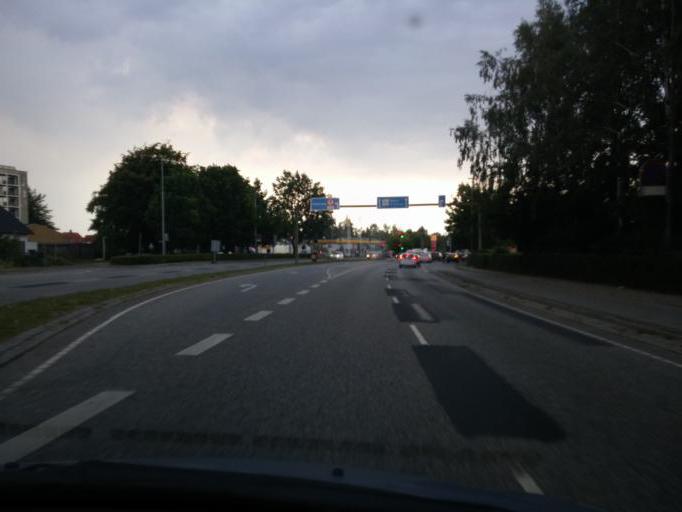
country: DK
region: South Denmark
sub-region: Odense Kommune
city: Odense
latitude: 55.3918
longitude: 10.4226
